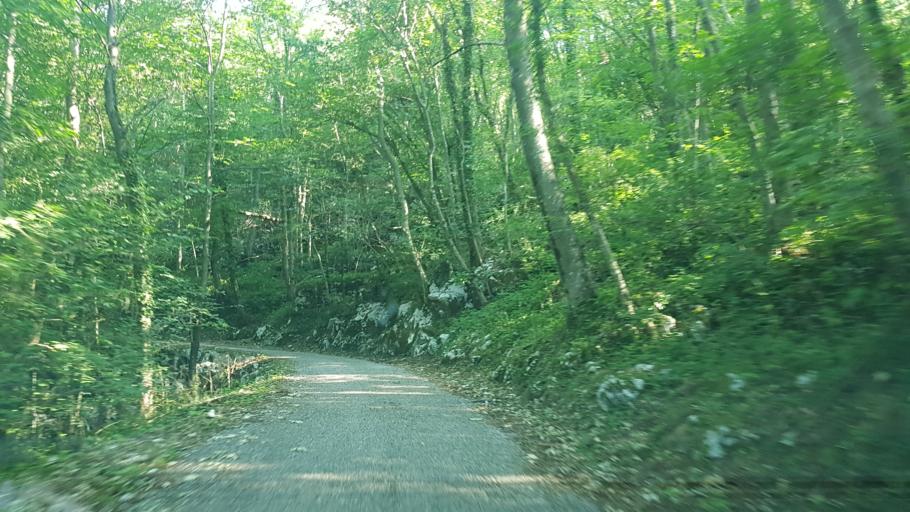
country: IT
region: Friuli Venezia Giulia
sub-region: Provincia di Udine
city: Nimis
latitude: 46.2289
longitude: 13.2559
